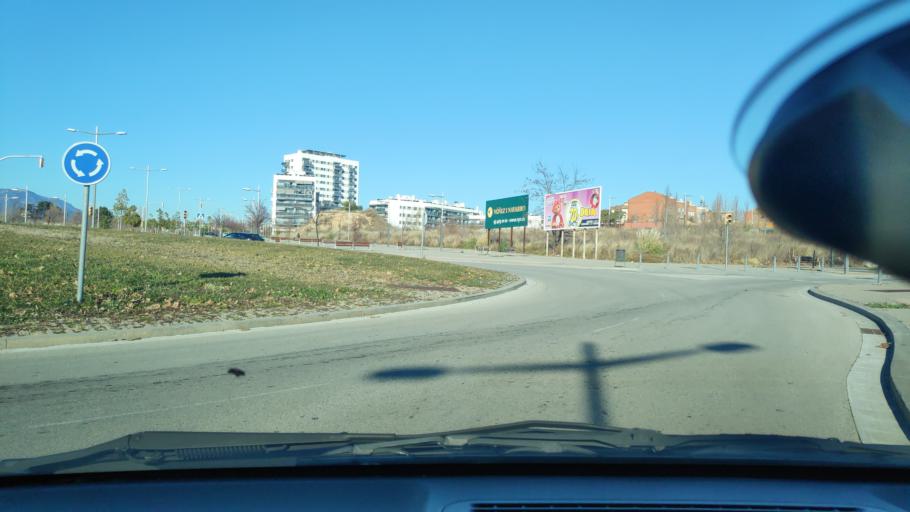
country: ES
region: Catalonia
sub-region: Provincia de Barcelona
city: Sant Quirze del Valles
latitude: 41.5470
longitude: 2.0794
